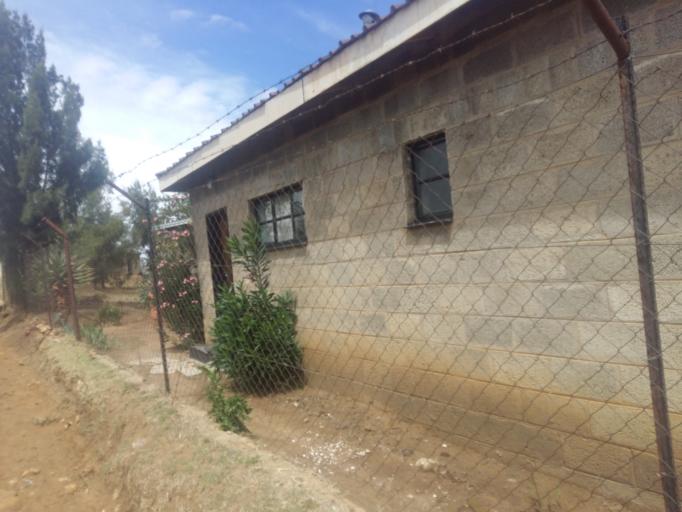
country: LS
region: Mafeteng
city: Mafeteng
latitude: -29.7011
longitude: 27.4344
